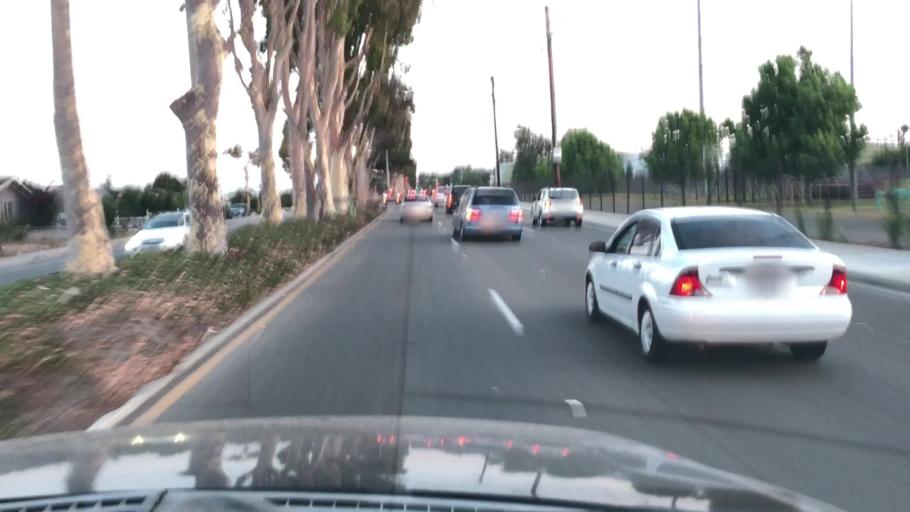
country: US
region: California
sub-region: Ventura County
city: Port Hueneme
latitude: 34.1718
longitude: -119.1951
